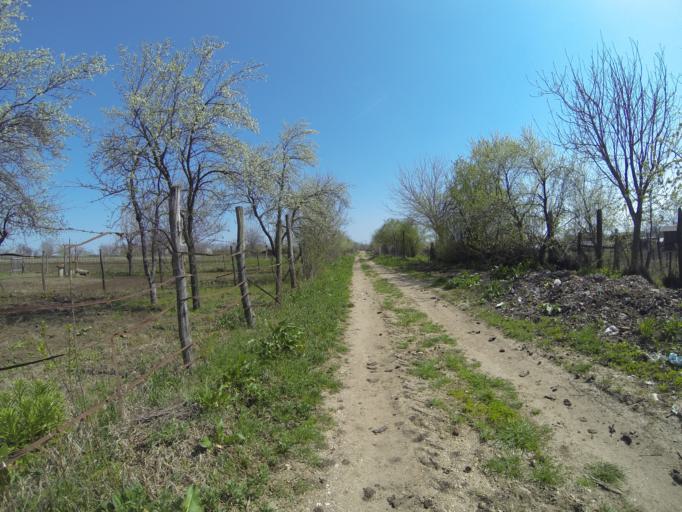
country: RO
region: Dolj
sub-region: Comuna Segarcea
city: Segarcea
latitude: 44.1029
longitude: 23.7316
